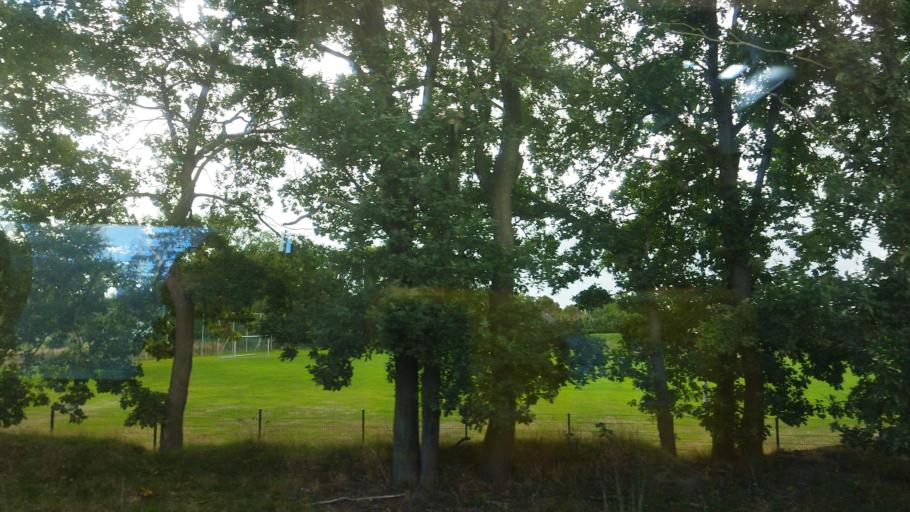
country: DE
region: Lower Saxony
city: Emsburen
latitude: 52.3951
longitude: 7.3073
